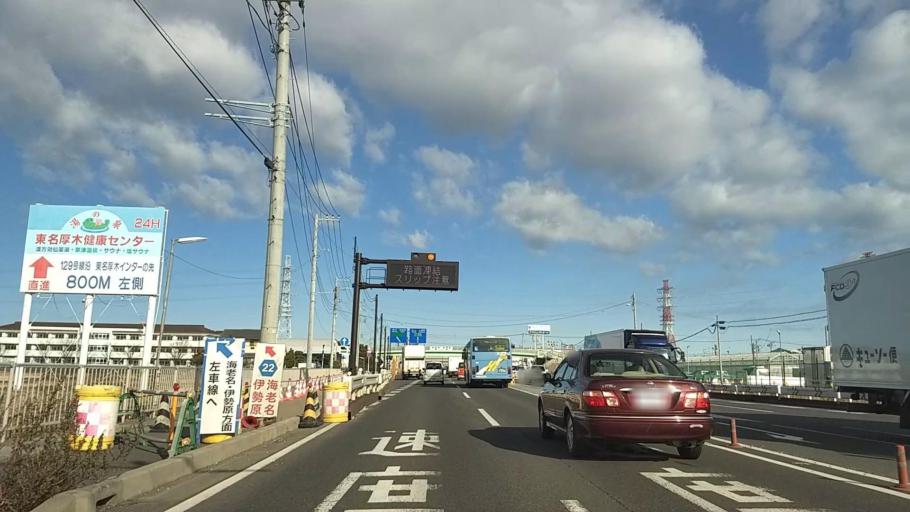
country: JP
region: Kanagawa
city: Atsugi
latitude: 35.4011
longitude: 139.3616
